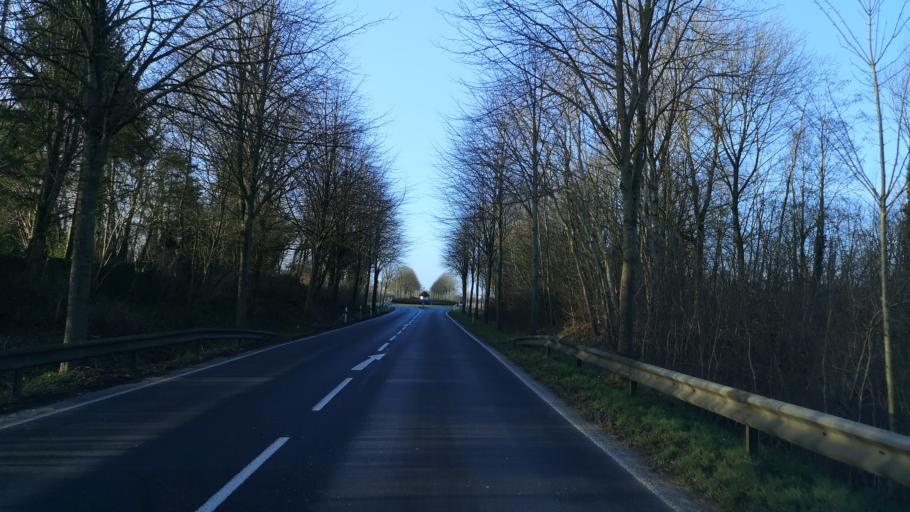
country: DE
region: Schleswig-Holstein
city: Tarp
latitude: 54.6682
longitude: 9.4115
